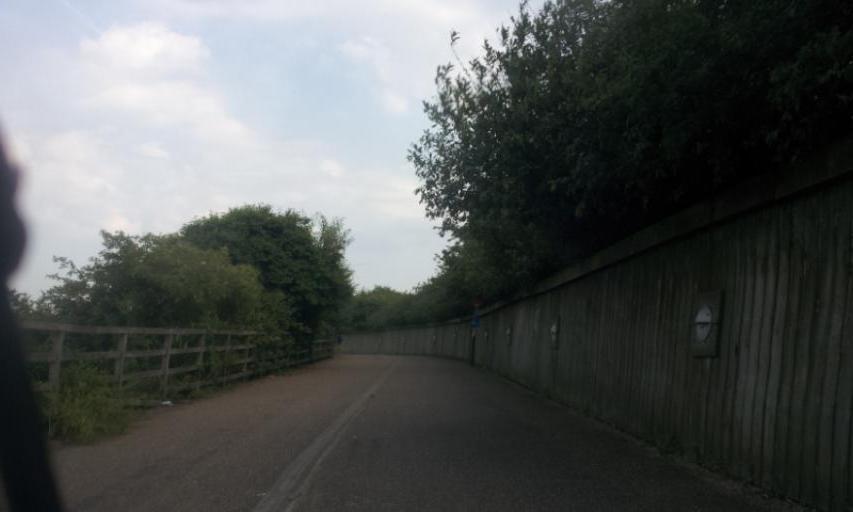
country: GB
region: England
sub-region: Greater London
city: Blackheath
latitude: 51.4957
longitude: 0.0162
